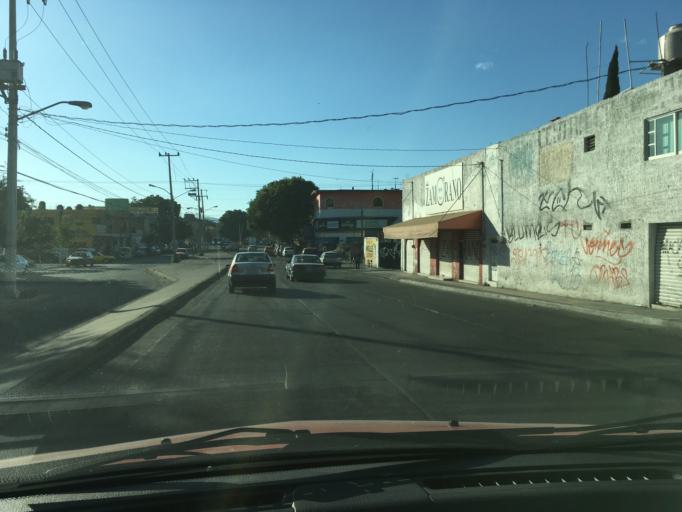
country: MX
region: Jalisco
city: Guadalajara
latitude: 20.6199
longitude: -103.3883
